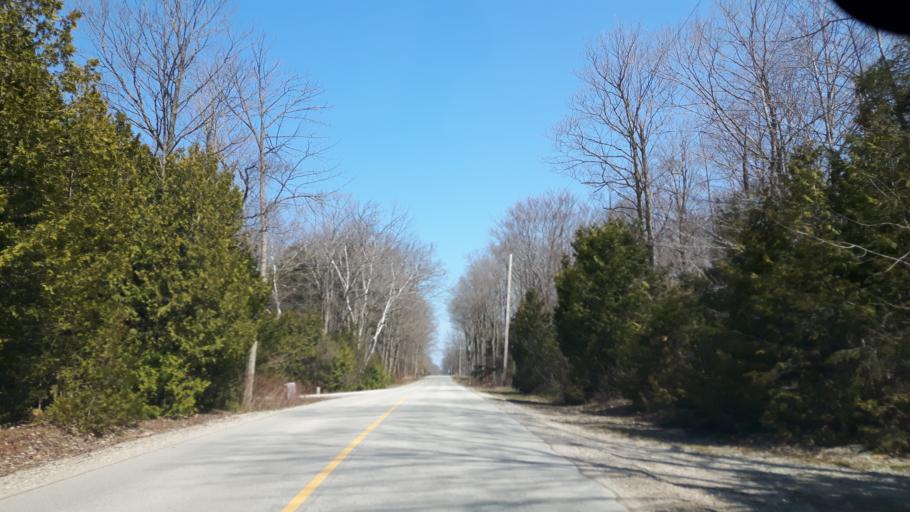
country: CA
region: Ontario
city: Bluewater
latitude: 43.5845
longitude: -81.6848
